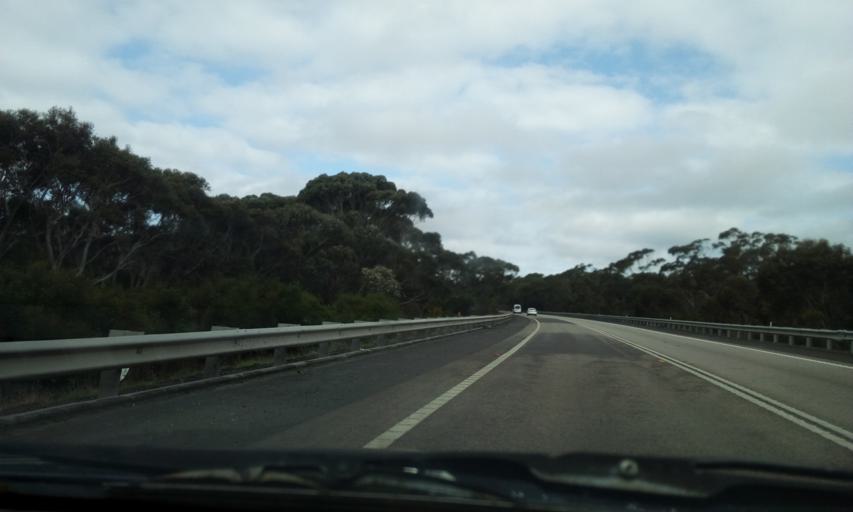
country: AU
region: New South Wales
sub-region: Wollongong
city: Bulli
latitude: -34.2494
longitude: 150.8515
